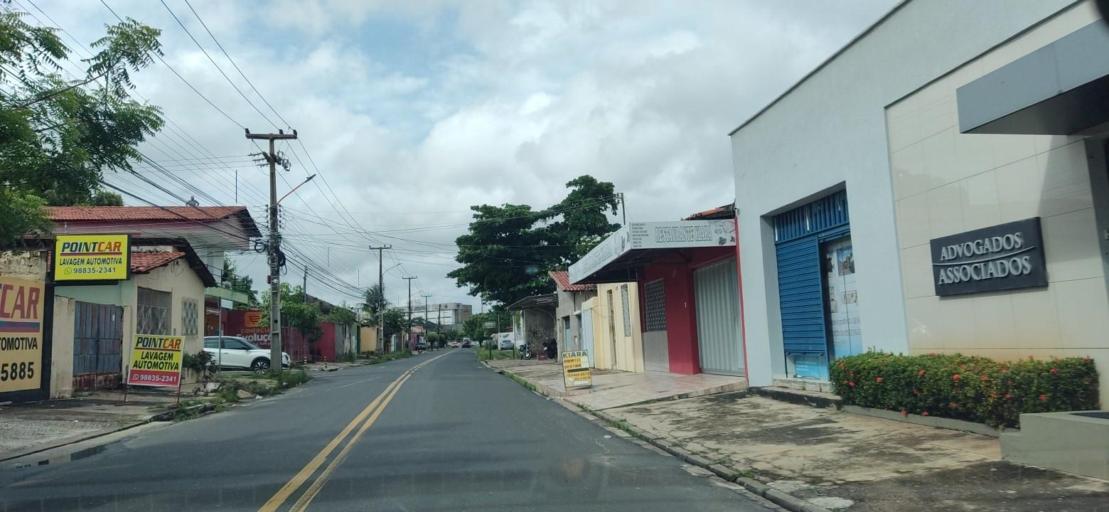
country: BR
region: Piaui
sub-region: Teresina
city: Teresina
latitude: -5.0791
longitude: -42.8067
